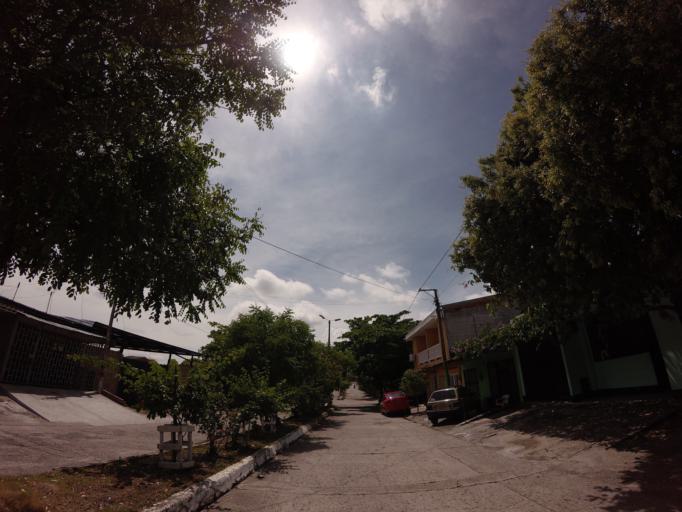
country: CO
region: Caldas
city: La Dorada
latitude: 5.4533
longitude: -74.6703
